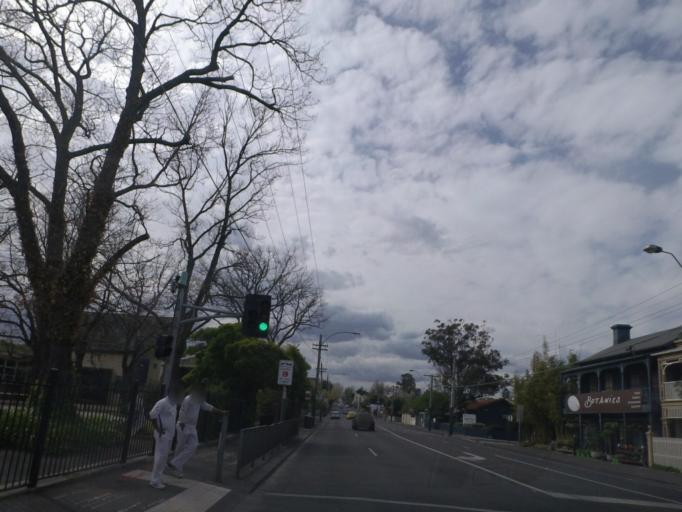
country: AU
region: Victoria
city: Windsor
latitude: -37.8414
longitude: 144.9858
